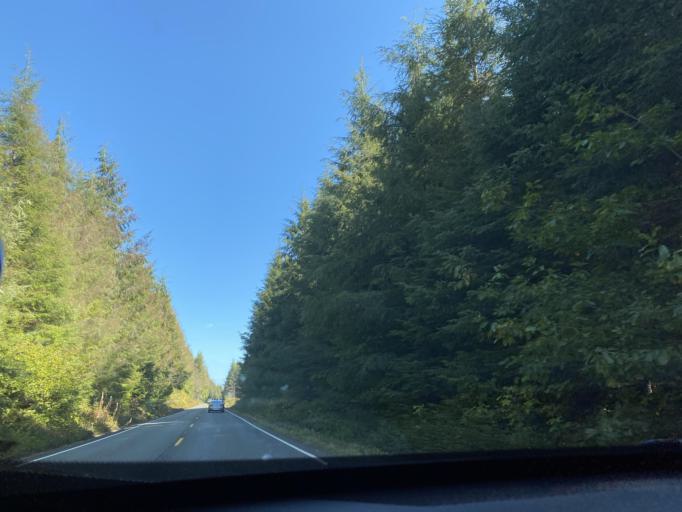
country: US
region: Washington
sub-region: Clallam County
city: Forks
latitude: 47.9183
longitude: -124.5213
